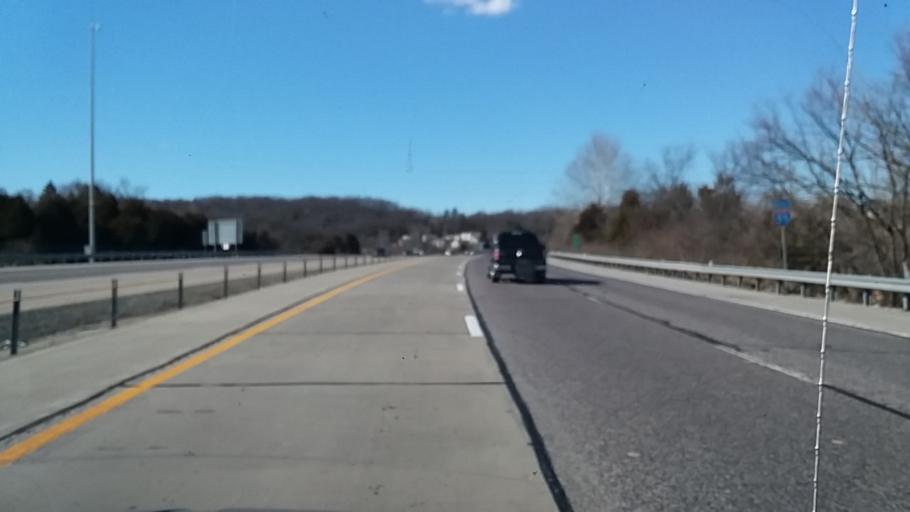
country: US
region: Missouri
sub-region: Jefferson County
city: Pevely
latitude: 38.2943
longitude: -90.4054
